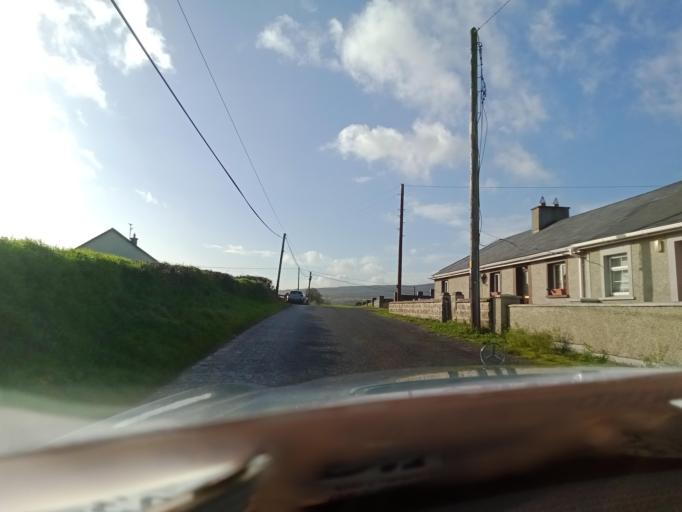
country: IE
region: Munster
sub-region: Waterford
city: Portlaw
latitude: 52.3263
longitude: -7.2872
